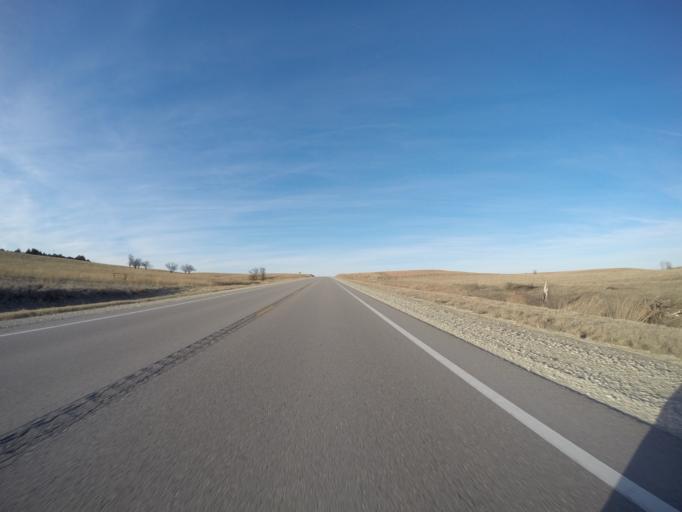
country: US
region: Kansas
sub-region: Marion County
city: Marion
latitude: 38.2809
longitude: -96.9632
